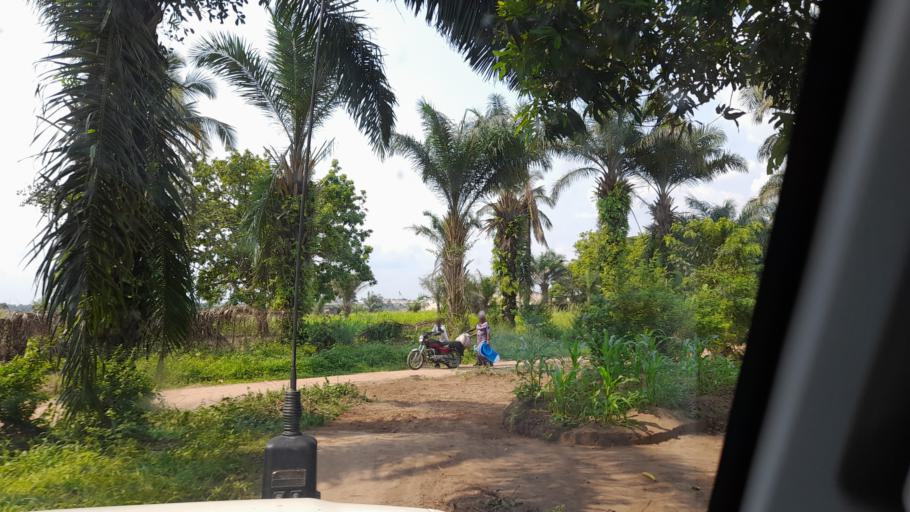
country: CD
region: Kasai-Occidental
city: Kananga
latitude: -5.9168
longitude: 22.4773
